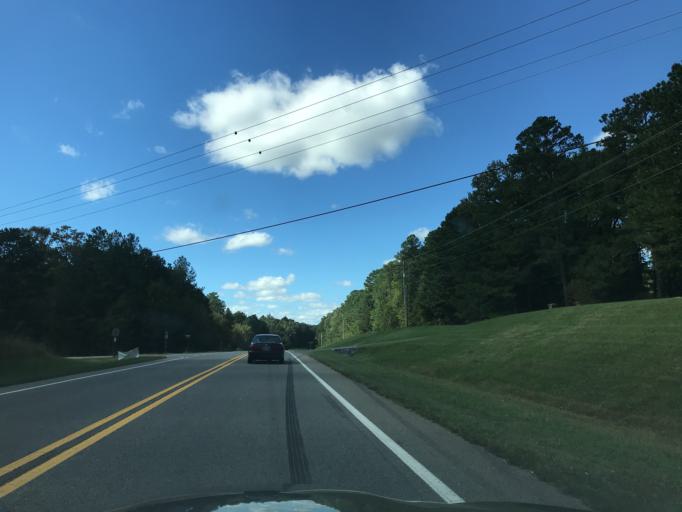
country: US
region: North Carolina
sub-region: Durham County
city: Gorman
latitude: 35.9801
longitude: -78.7269
